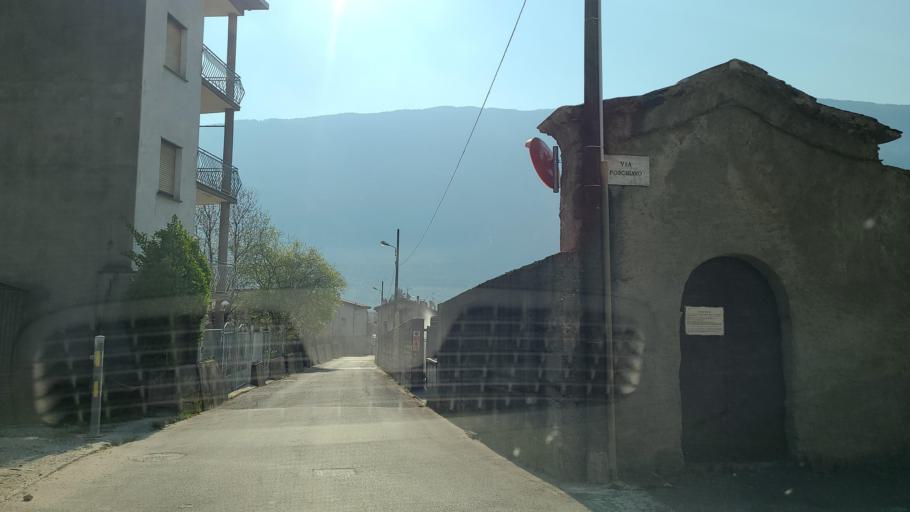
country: IT
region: Lombardy
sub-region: Provincia di Sondrio
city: Tirano
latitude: 46.2207
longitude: 10.1589
